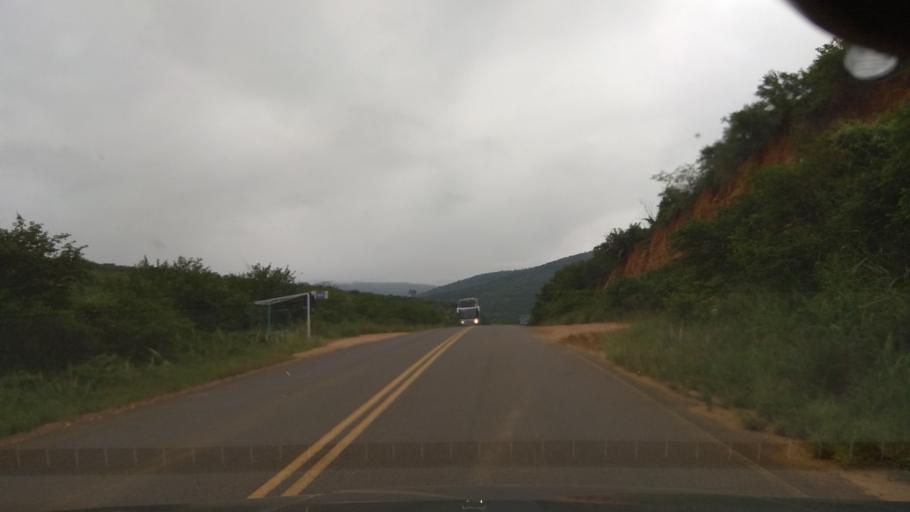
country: BR
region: Bahia
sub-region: Santa Ines
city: Santa Ines
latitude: -13.2522
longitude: -39.7789
